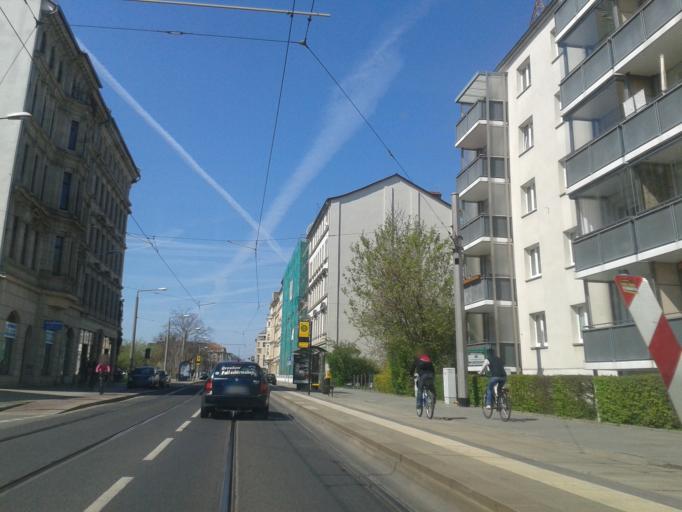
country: DE
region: Saxony
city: Dresden
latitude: 51.0524
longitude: 13.7276
